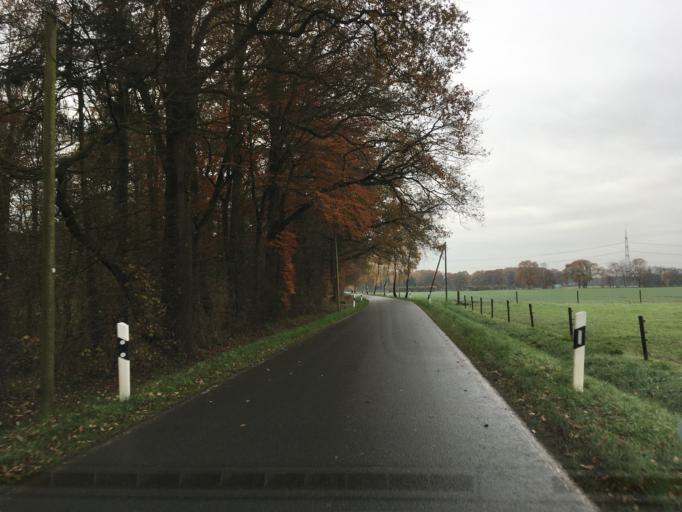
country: DE
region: North Rhine-Westphalia
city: Stadtlohn
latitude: 52.0181
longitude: 6.9757
